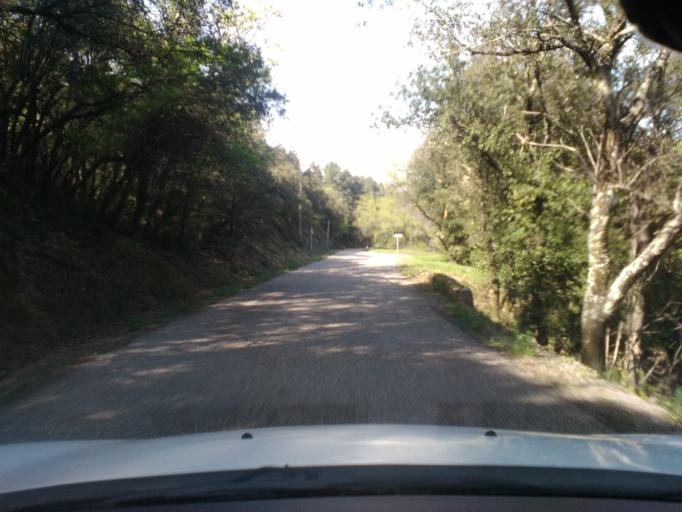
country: FR
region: Languedoc-Roussillon
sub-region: Departement du Gard
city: Lasalle
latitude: 44.0173
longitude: 3.8742
